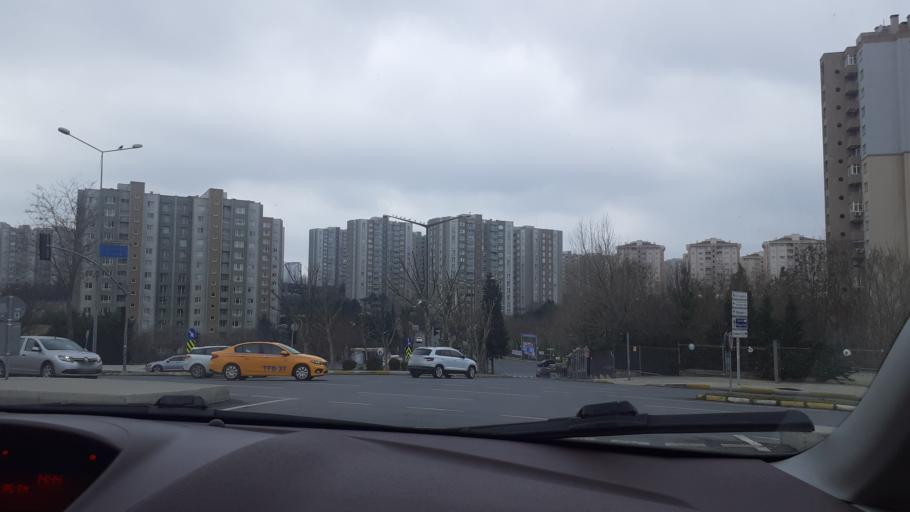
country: TR
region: Istanbul
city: Mahmutbey
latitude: 41.0483
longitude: 28.7867
